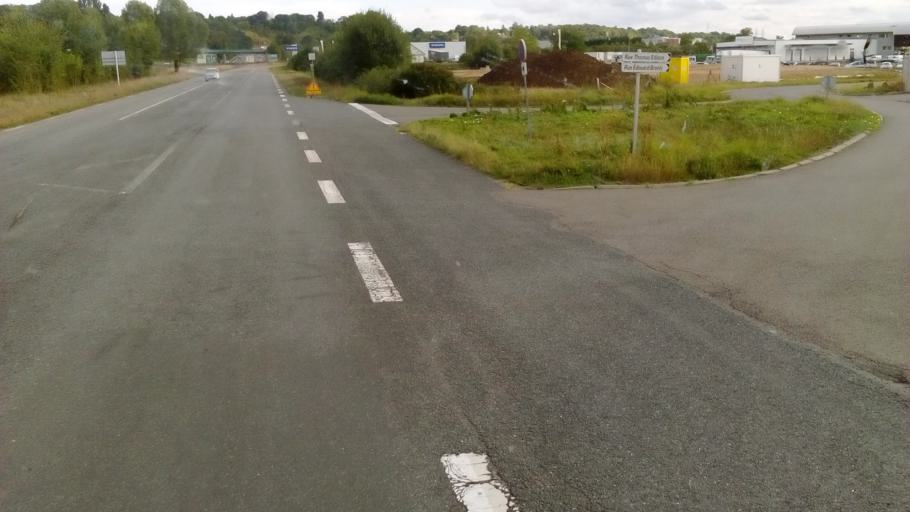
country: FR
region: Bourgogne
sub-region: Departement de la Nievre
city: Varennes-Vauzelles
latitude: 47.0477
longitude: 3.1309
